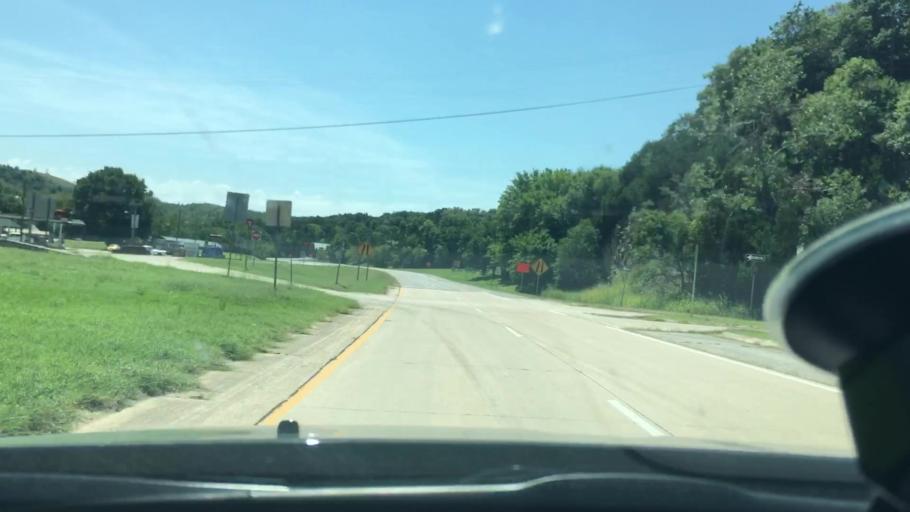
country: US
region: Oklahoma
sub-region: Murray County
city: Davis
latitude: 34.4493
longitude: -97.1355
